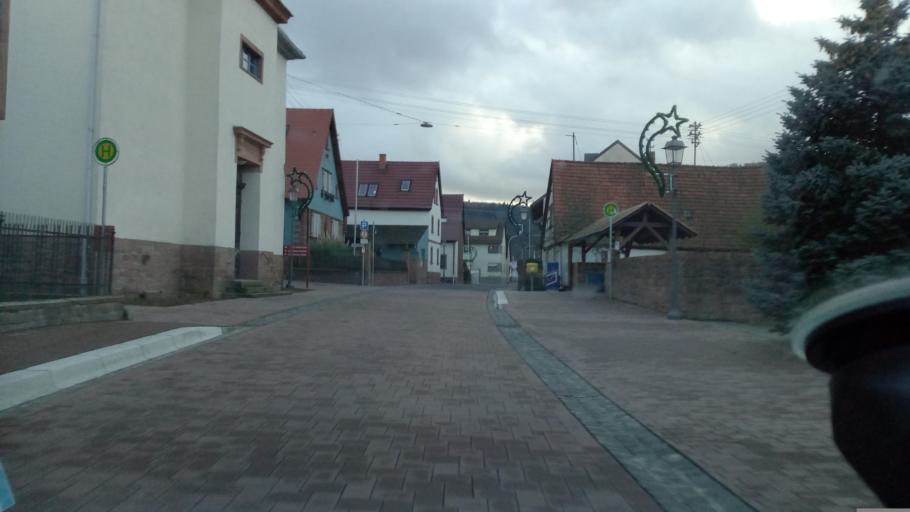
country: DE
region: Bavaria
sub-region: Regierungsbezirk Unterfranken
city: Faulbach
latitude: 49.7825
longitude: 9.4421
